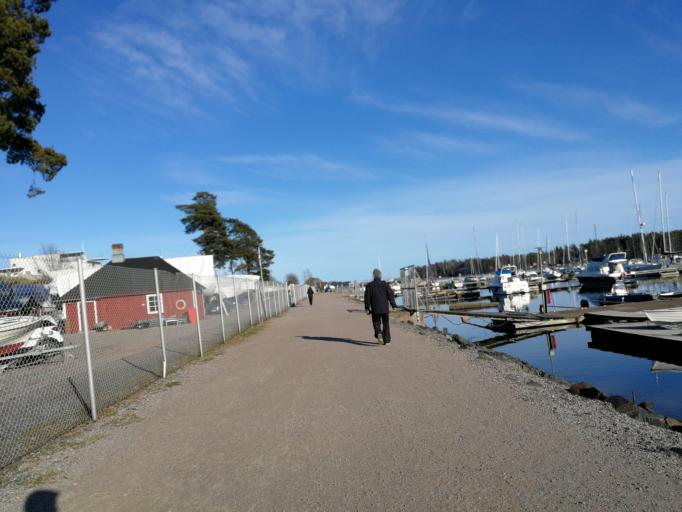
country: FI
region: Uusimaa
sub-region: Helsinki
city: Vantaa
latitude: 60.2000
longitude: 25.1371
